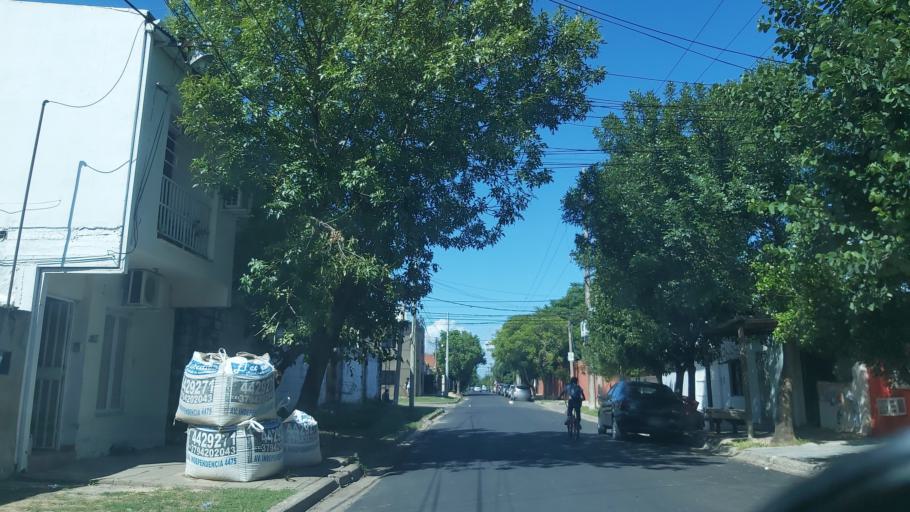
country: AR
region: Corrientes
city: Corrientes
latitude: -27.4776
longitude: -58.8473
